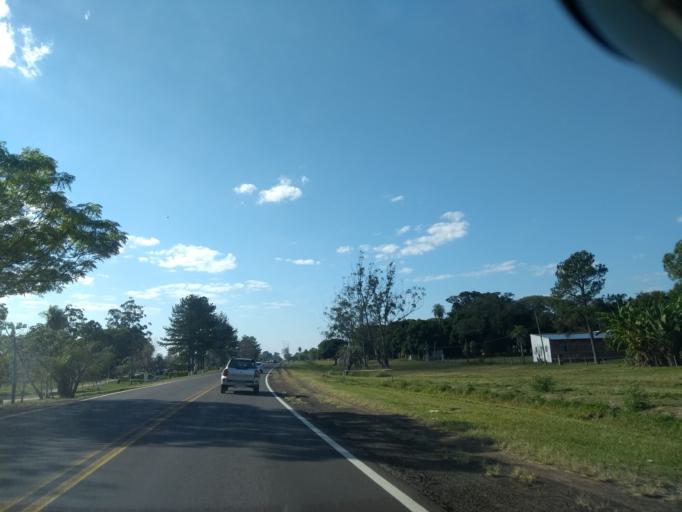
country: AR
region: Corrientes
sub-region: Departamento de Itati
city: Itati
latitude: -27.3660
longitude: -58.3040
